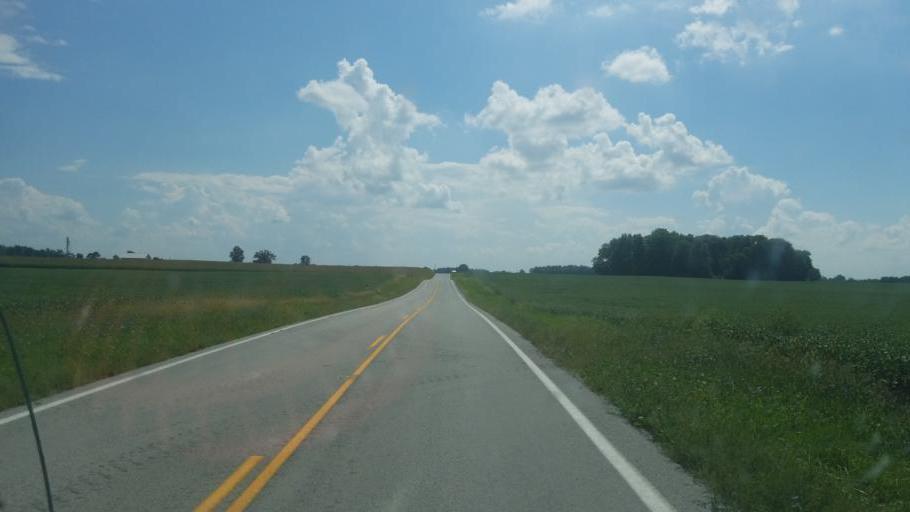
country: US
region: Ohio
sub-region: Hardin County
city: Forest
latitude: 40.8531
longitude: -83.4575
